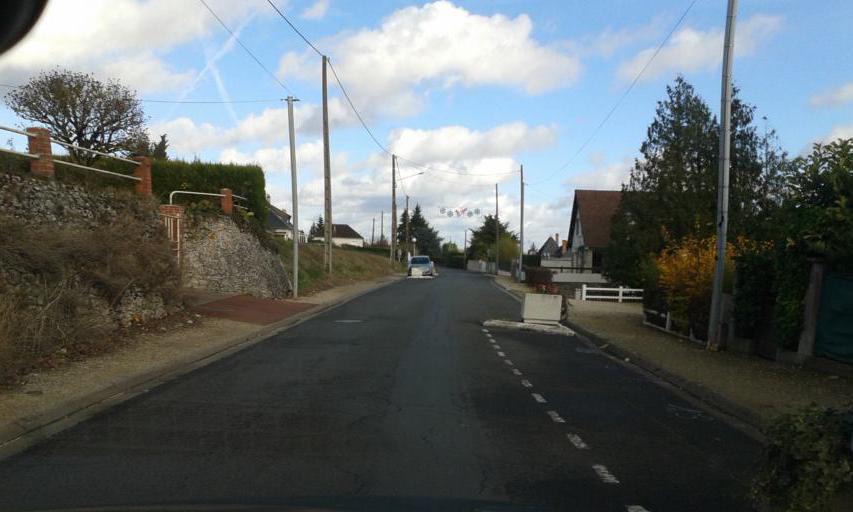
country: FR
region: Centre
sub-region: Departement du Loiret
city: Tavers
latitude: 47.7593
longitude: 1.6187
